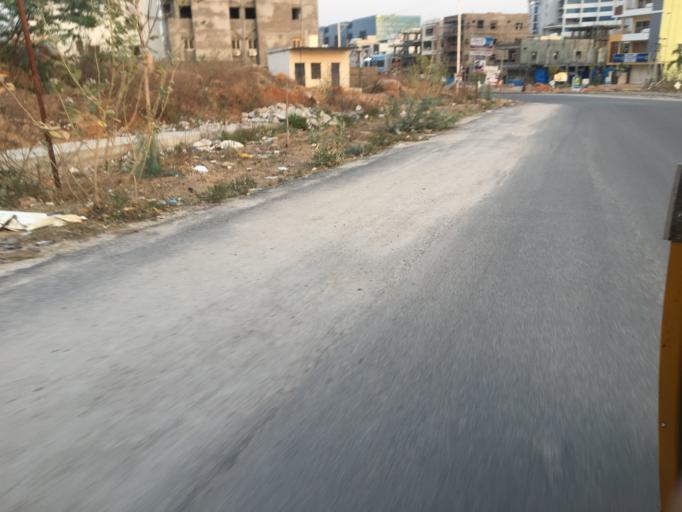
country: IN
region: Telangana
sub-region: Medak
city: Serilingampalle
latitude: 17.4302
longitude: 78.3314
